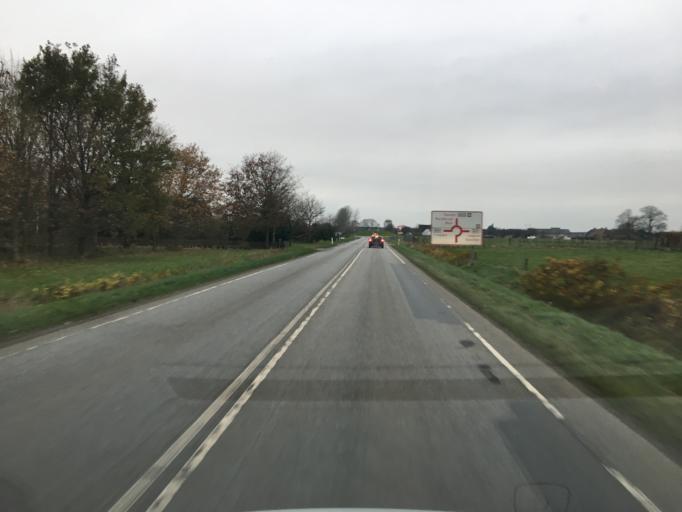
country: DK
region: South Denmark
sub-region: Aabenraa Kommune
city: Tinglev
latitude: 54.9769
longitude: 9.1458
